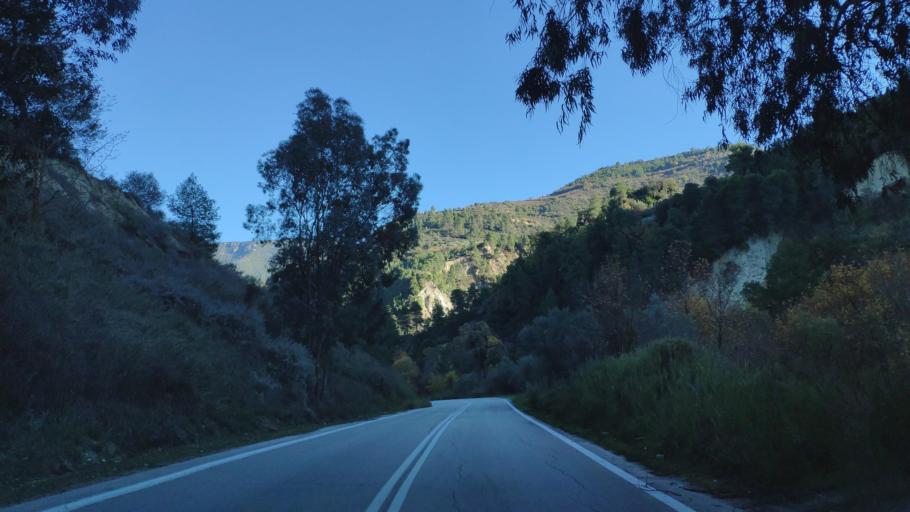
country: GR
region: Peloponnese
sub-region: Nomos Korinthias
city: Xylokastro
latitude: 38.0091
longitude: 22.5302
